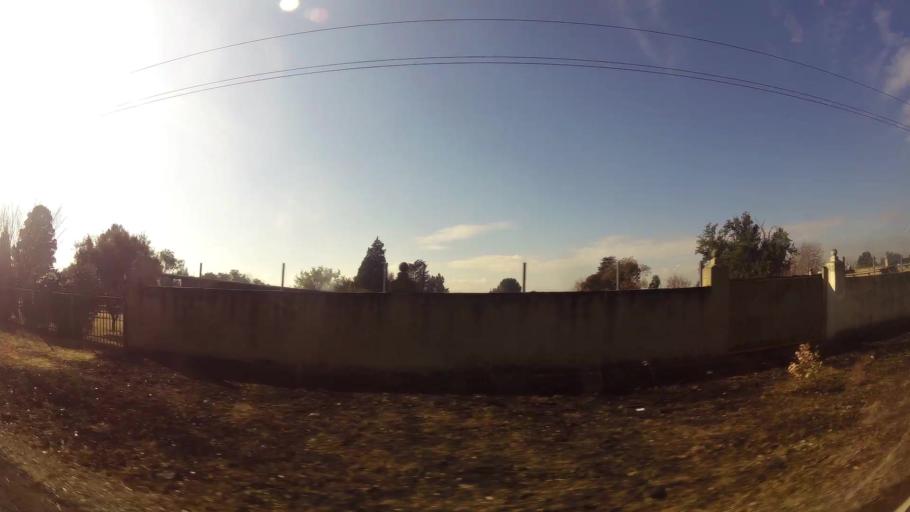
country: ZA
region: Gauteng
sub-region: Sedibeng District Municipality
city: Meyerton
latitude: -26.4980
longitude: 28.0596
